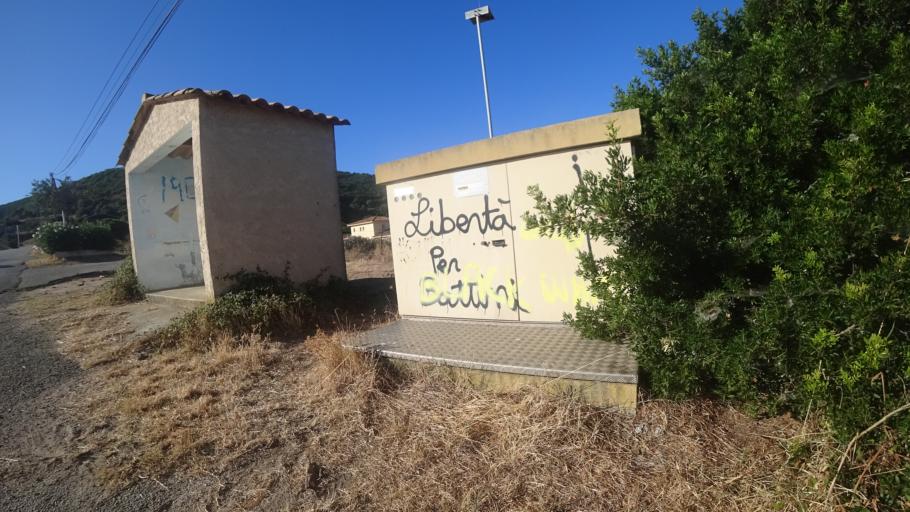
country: FR
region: Corsica
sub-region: Departement de la Corse-du-Sud
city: Alata
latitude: 41.9736
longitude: 8.6894
